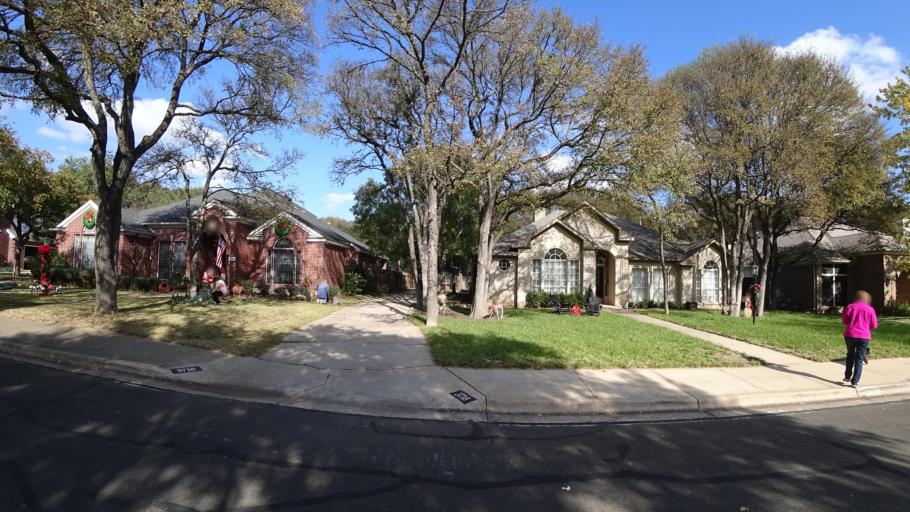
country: US
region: Texas
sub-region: Travis County
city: Shady Hollow
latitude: 30.1814
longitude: -97.8571
